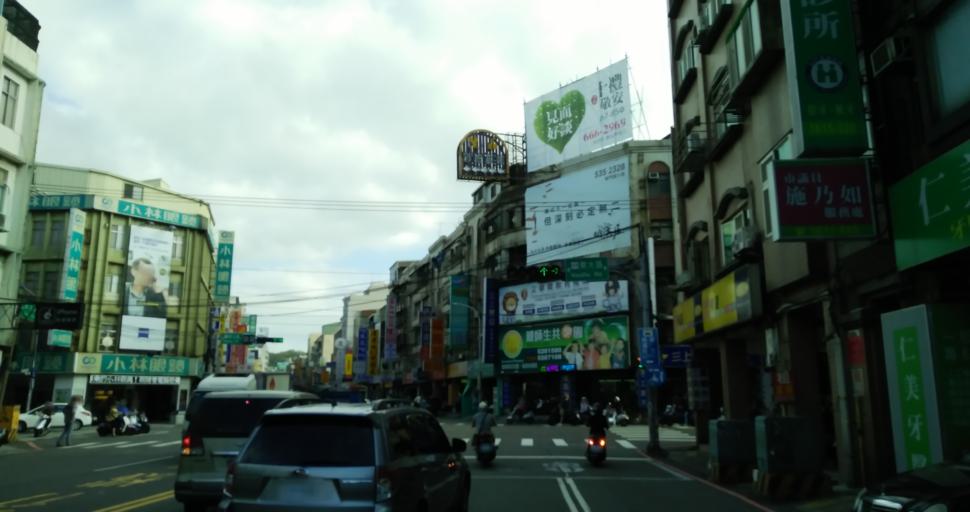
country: TW
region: Taiwan
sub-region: Hsinchu
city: Hsinchu
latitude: 24.7976
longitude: 120.9689
